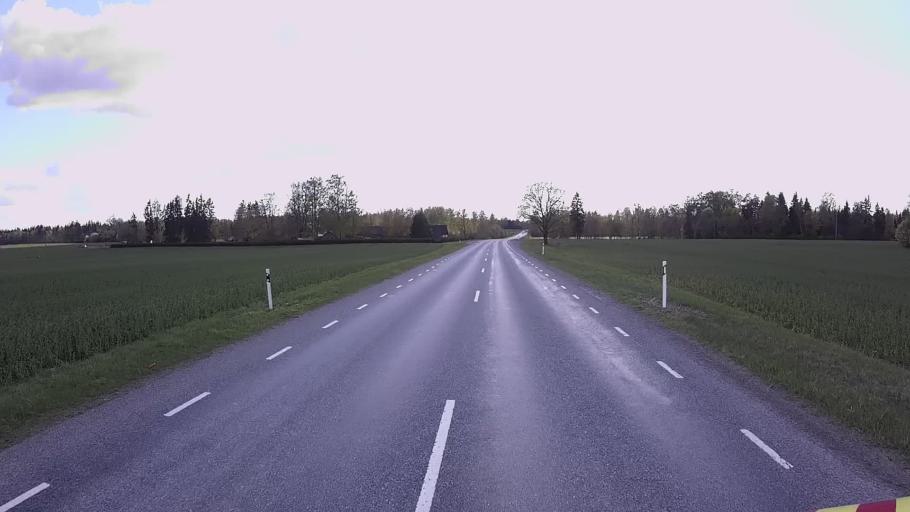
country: EE
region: Jogevamaa
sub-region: Poltsamaa linn
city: Poltsamaa
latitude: 58.6837
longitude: 26.0791
